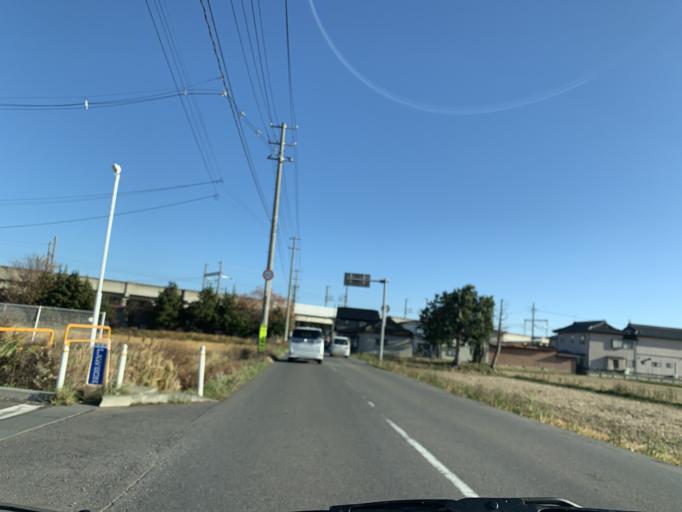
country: JP
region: Iwate
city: Kitakami
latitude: 39.2547
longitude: 141.1100
